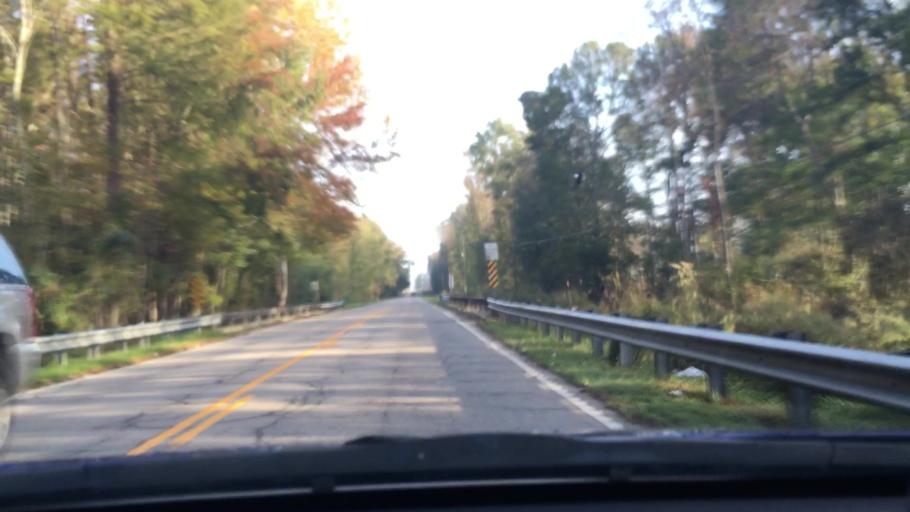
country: US
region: South Carolina
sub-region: Sumter County
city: East Sumter
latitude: 33.9642
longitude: -80.3017
